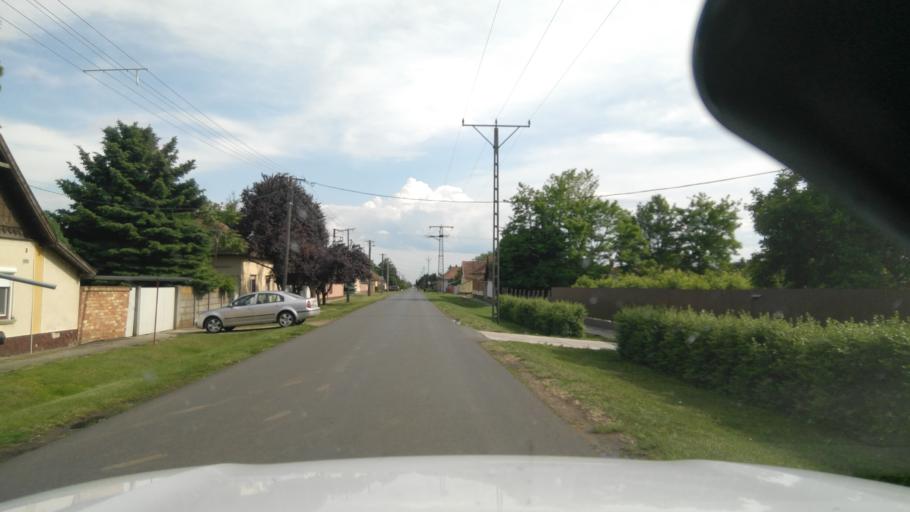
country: HU
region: Bekes
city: Ujkigyos
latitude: 46.5942
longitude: 21.0337
